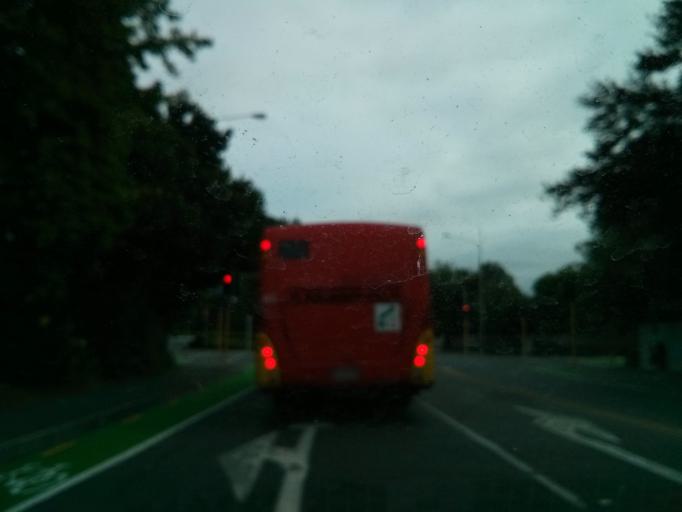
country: NZ
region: Canterbury
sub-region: Christchurch City
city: Christchurch
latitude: -43.5228
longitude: 172.5892
